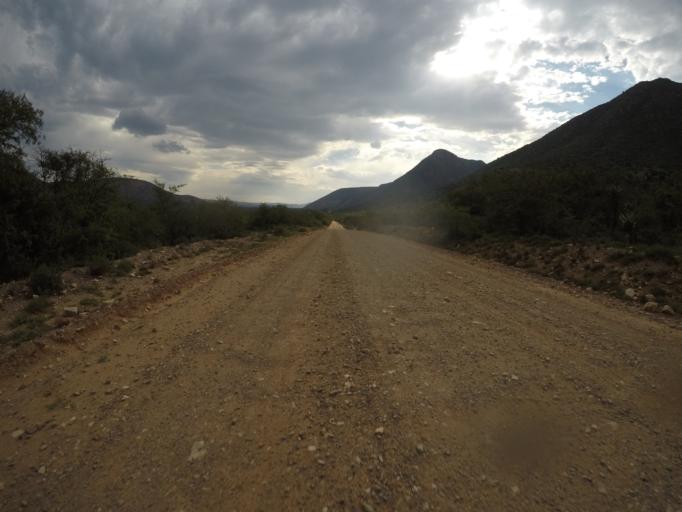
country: ZA
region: Eastern Cape
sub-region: Cacadu District Municipality
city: Kareedouw
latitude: -33.5810
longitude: 24.1560
